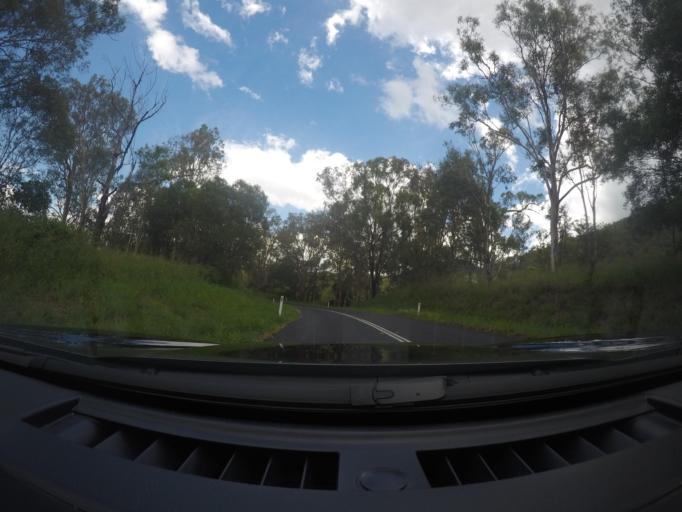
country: AU
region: Queensland
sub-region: Moreton Bay
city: Woodford
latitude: -27.0794
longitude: 152.5608
